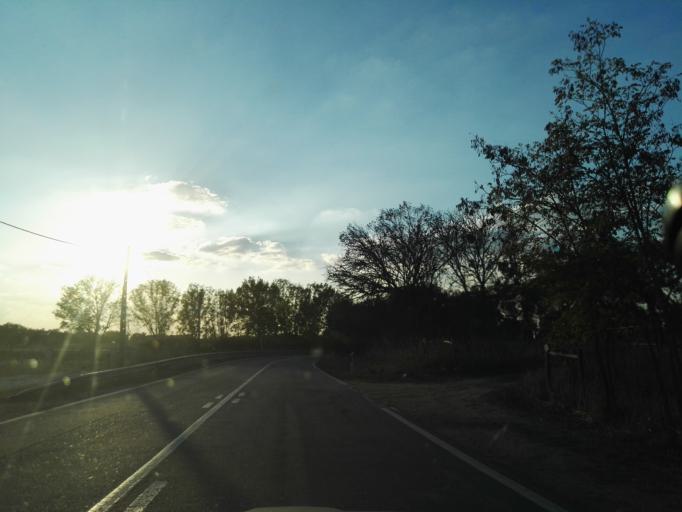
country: PT
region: Evora
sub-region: Mora
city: Mora
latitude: 38.8940
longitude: -8.0340
